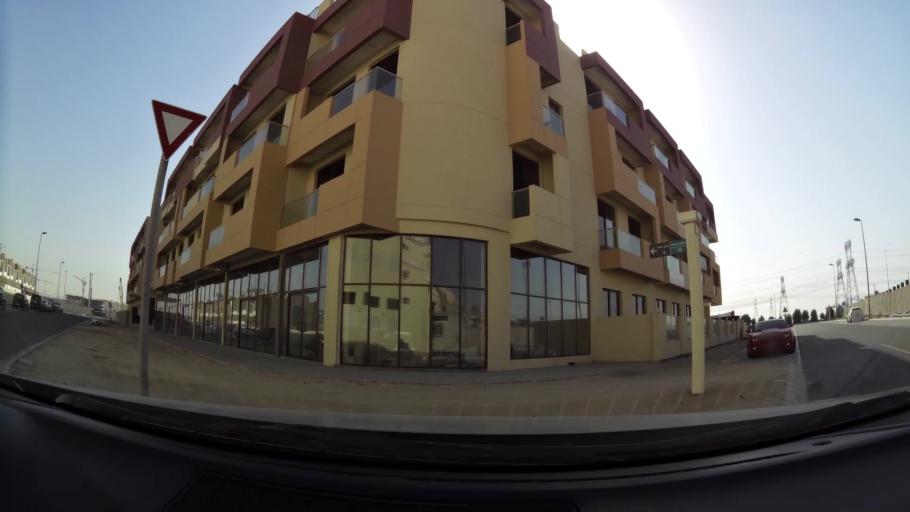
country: AE
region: Dubai
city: Dubai
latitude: 25.0660
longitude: 55.2036
